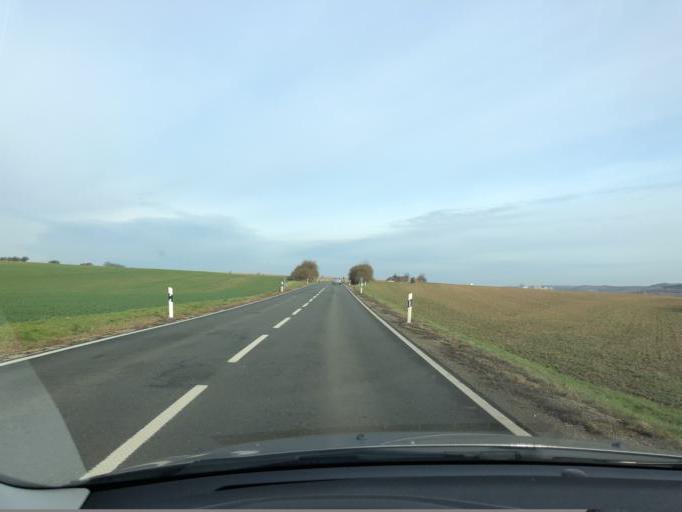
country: DE
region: Saxony-Anhalt
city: Laucha
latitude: 51.2319
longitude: 11.6675
